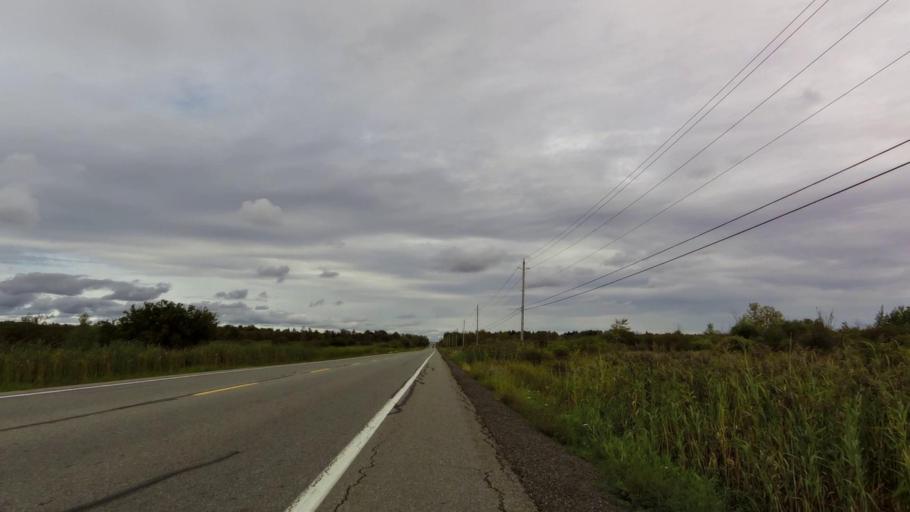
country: CA
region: Ontario
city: Ottawa
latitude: 45.3014
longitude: -75.6694
